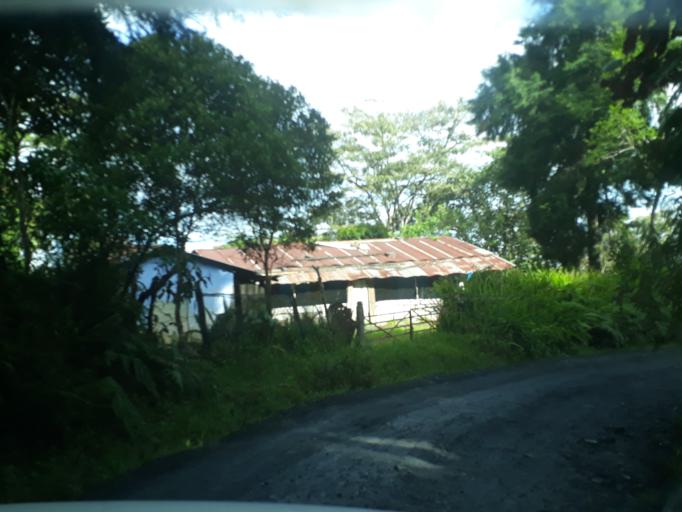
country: CO
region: Cundinamarca
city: La Mesa
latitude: 5.3327
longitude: -74.0571
